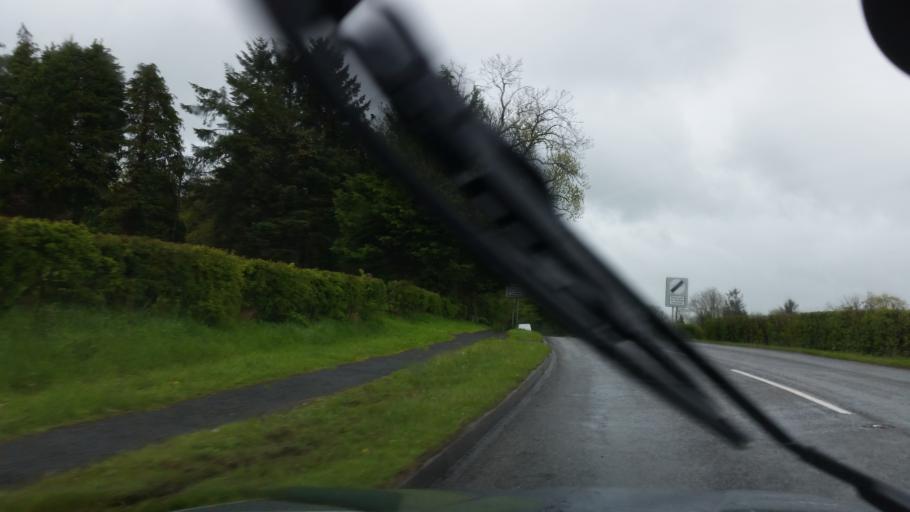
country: GB
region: Northern Ireland
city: Fintona
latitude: 54.4955
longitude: -7.3098
